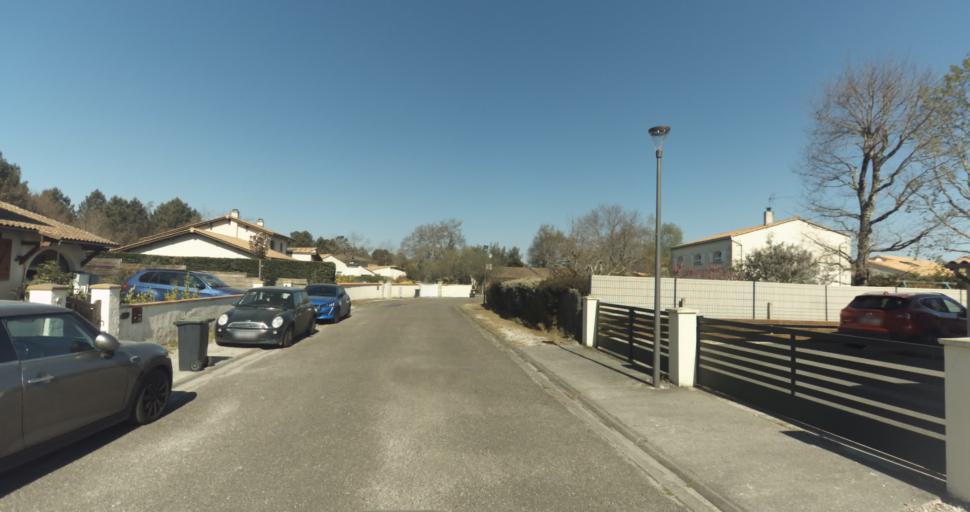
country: FR
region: Aquitaine
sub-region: Departement de la Gironde
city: Martignas-sur-Jalle
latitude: 44.8002
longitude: -0.7929
